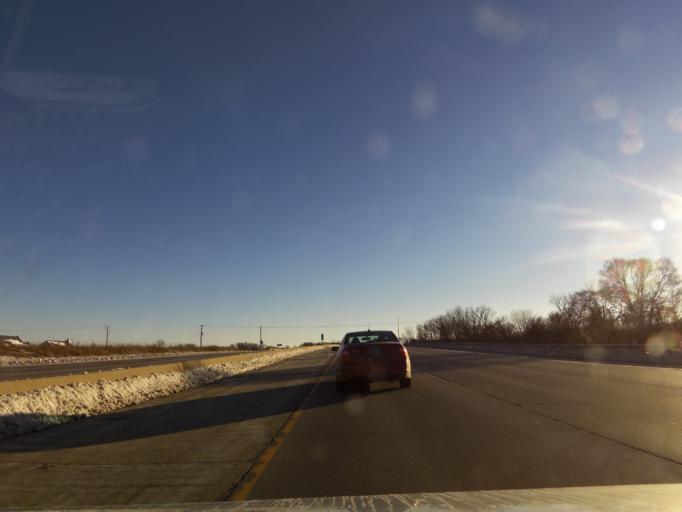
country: US
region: Wisconsin
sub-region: Racine County
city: Caledonia
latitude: 42.8598
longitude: -87.9379
